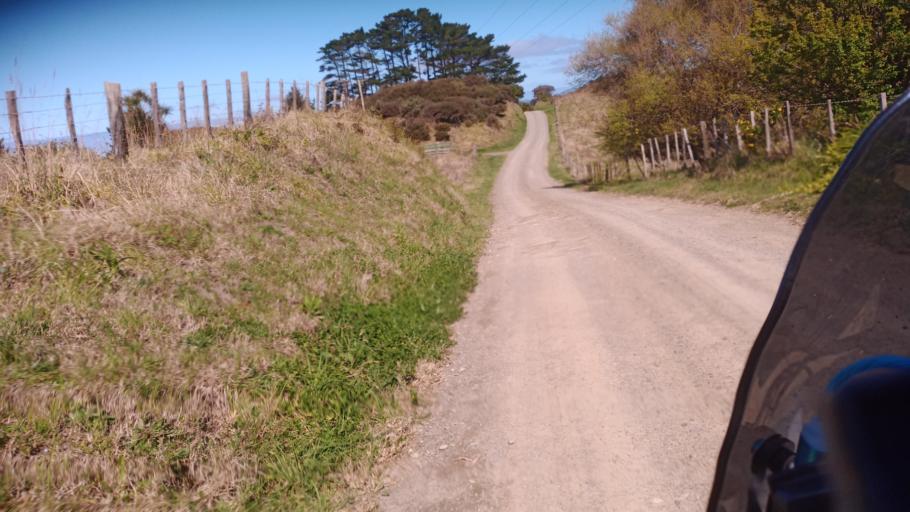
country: NZ
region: Gisborne
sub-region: Gisborne District
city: Gisborne
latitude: -39.0100
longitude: 177.8864
